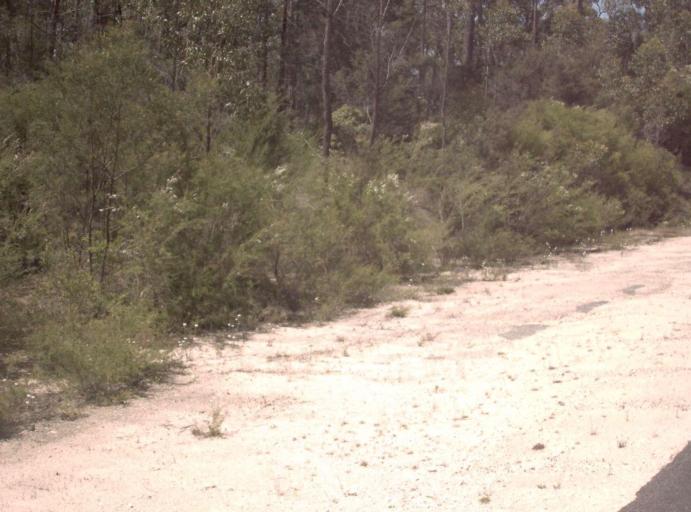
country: AU
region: New South Wales
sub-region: Bombala
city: Bombala
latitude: -37.5686
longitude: 149.2141
